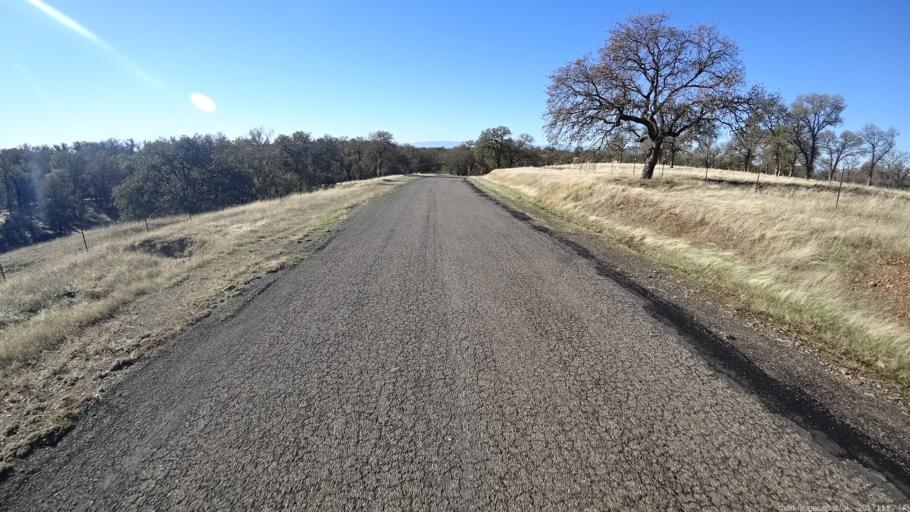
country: US
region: California
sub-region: Shasta County
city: Cottonwood
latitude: 40.4235
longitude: -122.1873
